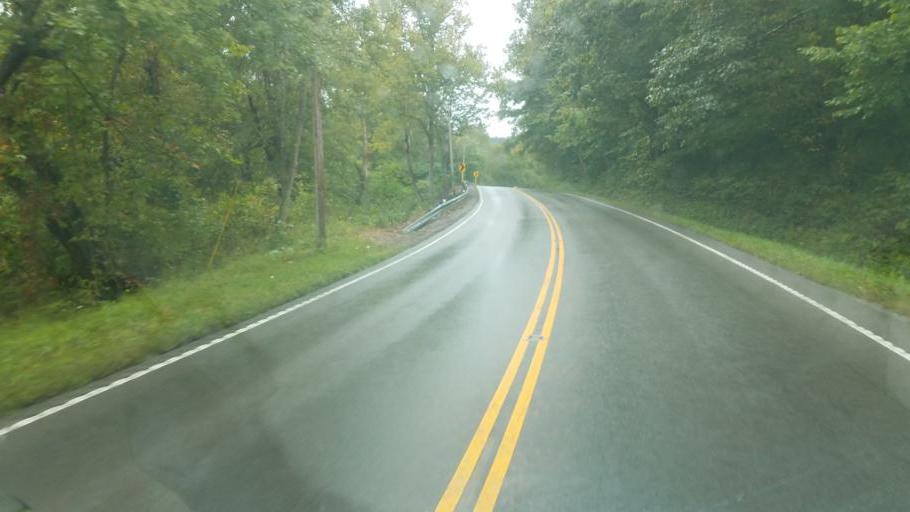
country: US
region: Ohio
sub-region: Jackson County
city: Oak Hill
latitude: 38.8285
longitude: -82.6615
